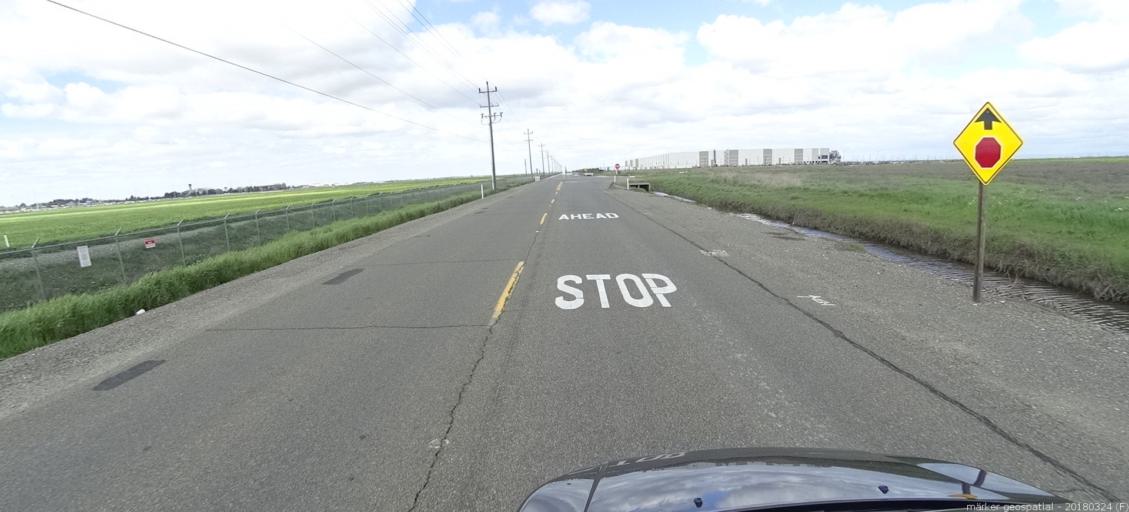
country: US
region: California
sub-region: Yolo County
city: West Sacramento
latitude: 38.6750
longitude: -121.5765
